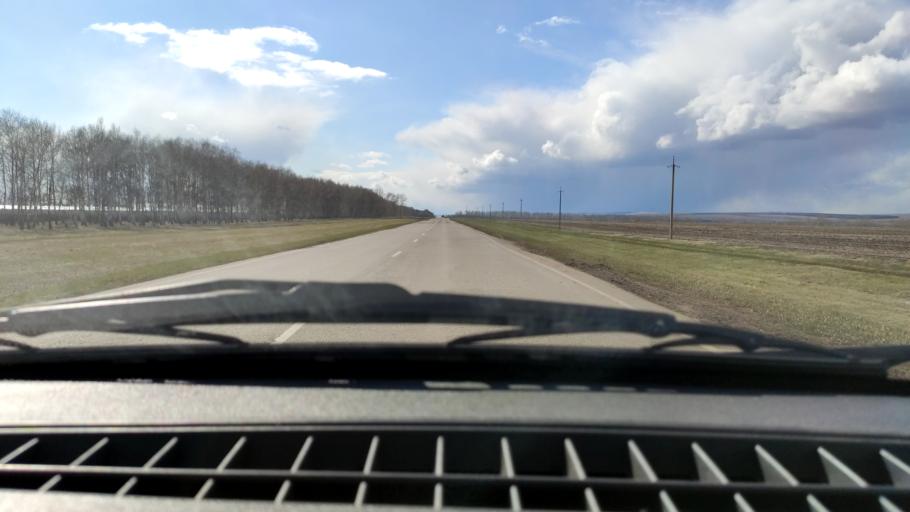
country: RU
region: Bashkortostan
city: Kushnarenkovo
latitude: 55.1042
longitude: 55.0238
